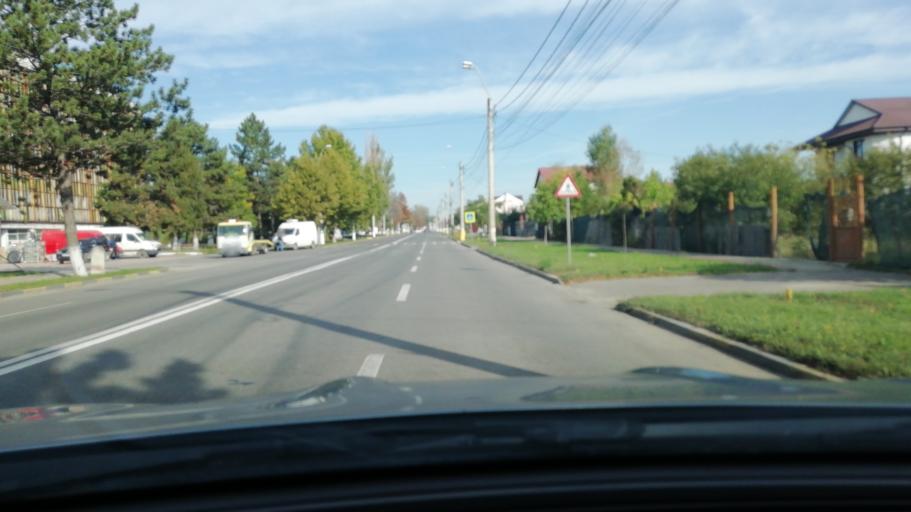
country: RO
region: Galati
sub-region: Municipiul Tecuci
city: Tecuci
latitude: 45.8229
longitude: 27.4386
